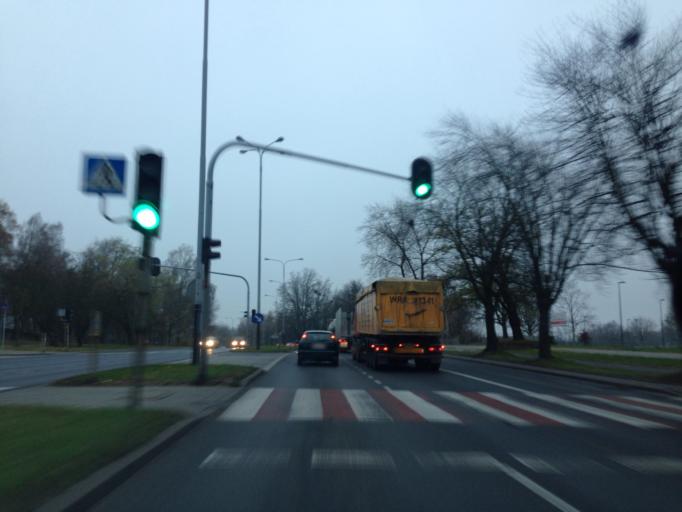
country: PL
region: Lodz Voivodeship
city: Lodz
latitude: 51.7879
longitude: 19.4846
